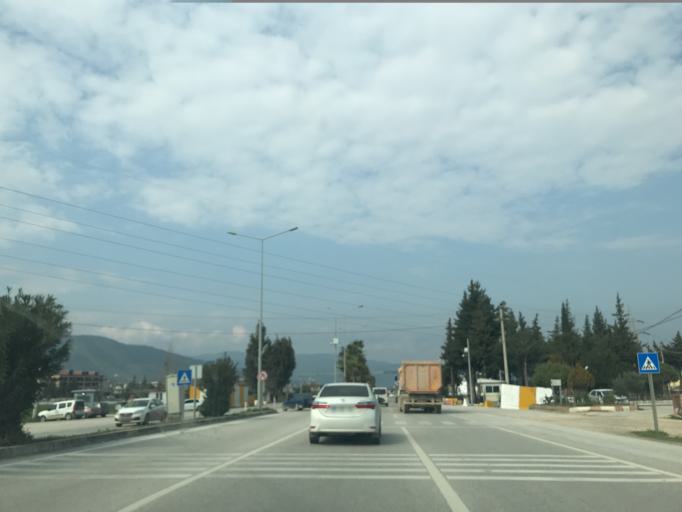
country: TR
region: Hatay
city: Anayazi
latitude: 36.3126
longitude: 36.2008
